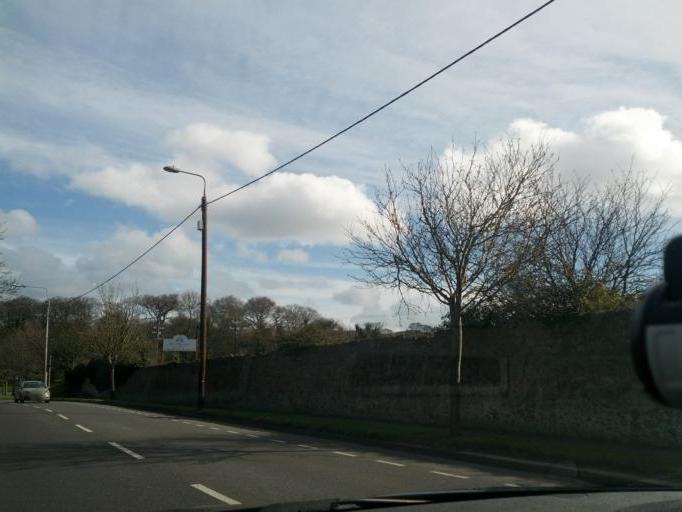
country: IE
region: Leinster
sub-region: Fingal County
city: Howth
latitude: 53.3893
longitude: -6.0824
